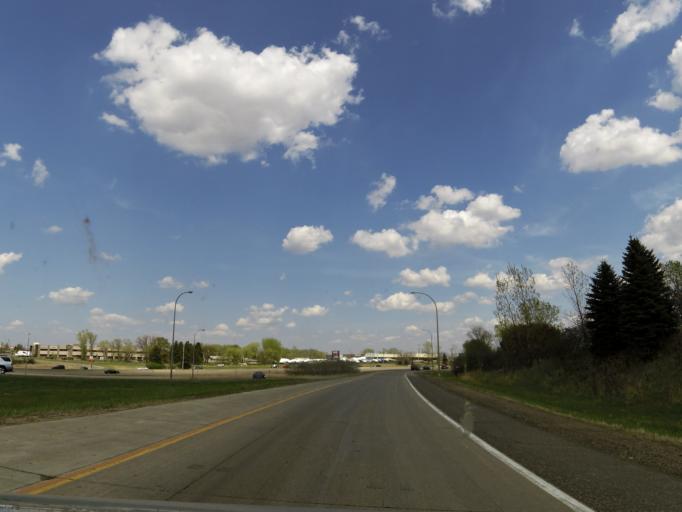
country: US
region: Minnesota
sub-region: Washington County
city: Oakdale
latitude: 44.9469
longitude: -92.9580
